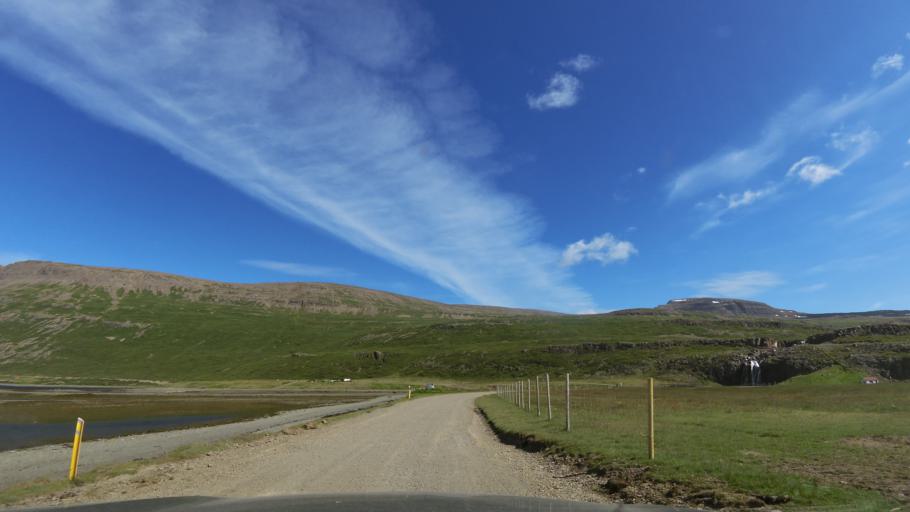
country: IS
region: Westfjords
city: Isafjoerdur
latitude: 65.6038
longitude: -23.5449
